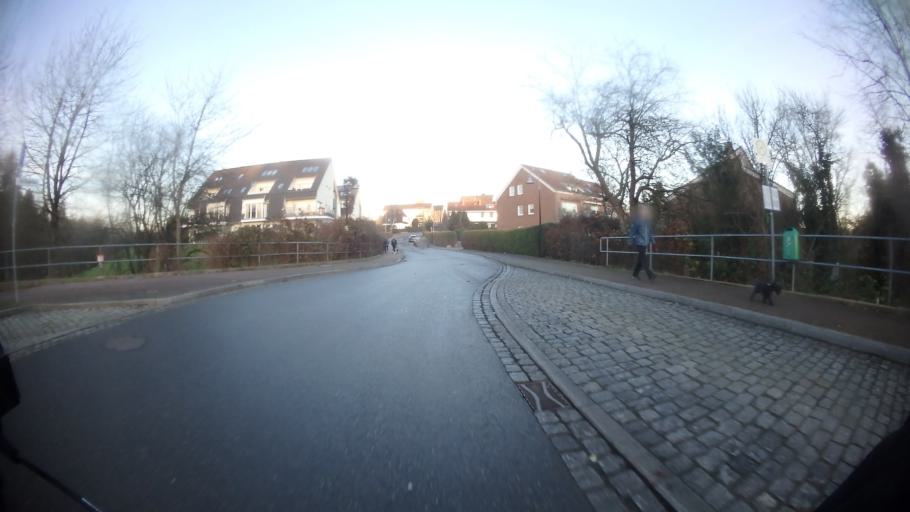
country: DE
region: Schleswig-Holstein
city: Scharbeutz
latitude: 54.0199
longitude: 10.7456
